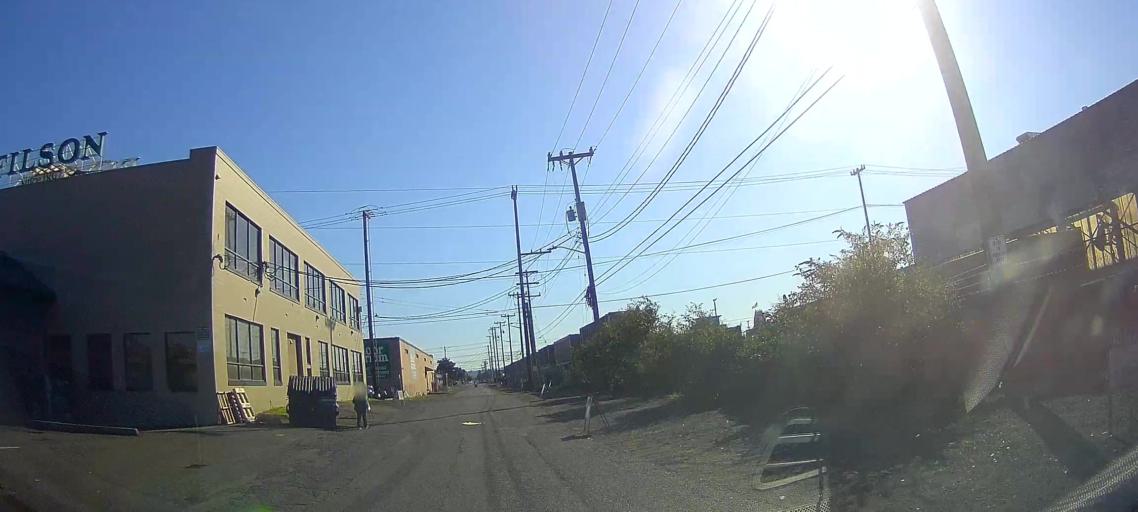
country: US
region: Washington
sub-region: King County
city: Seattle
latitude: 47.5890
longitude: -122.3300
